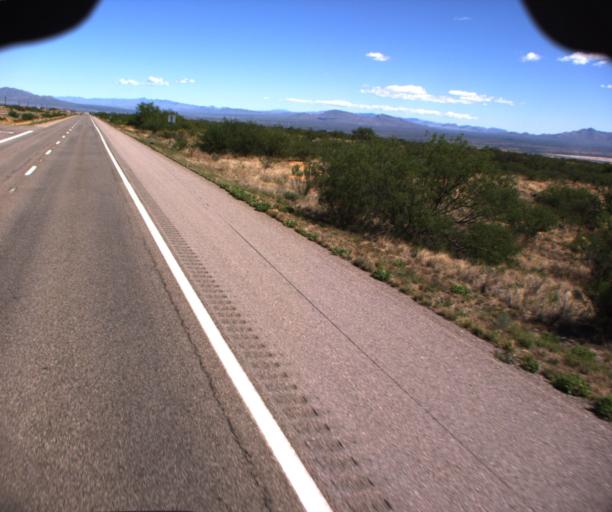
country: US
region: Arizona
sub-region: Cochise County
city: Whetstone
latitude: 31.9132
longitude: -110.3410
